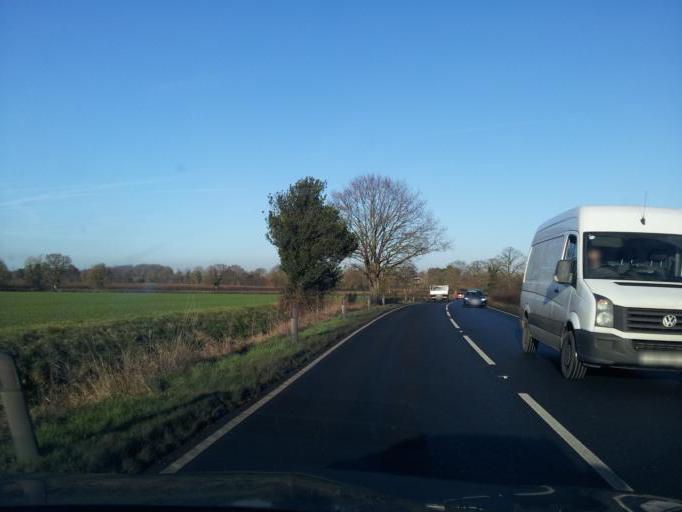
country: GB
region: England
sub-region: Suffolk
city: Lavenham
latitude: 52.1519
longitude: 0.7575
